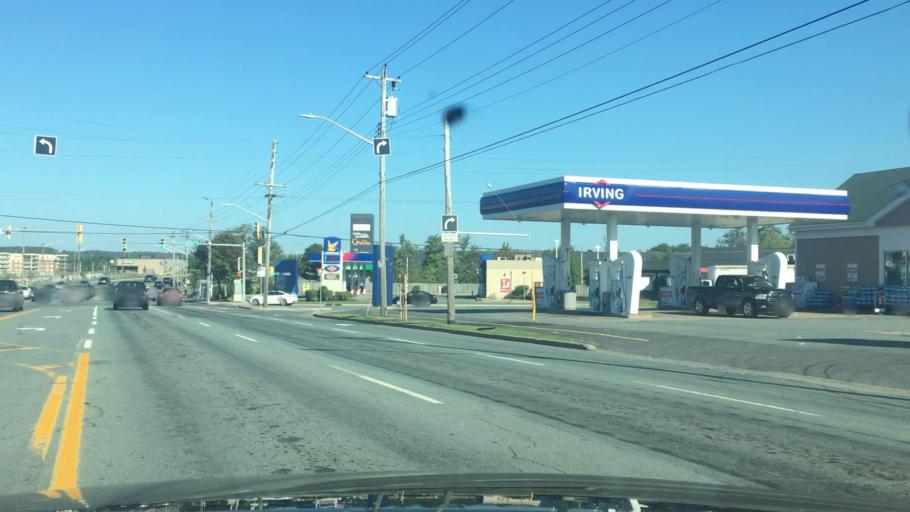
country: CA
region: Nova Scotia
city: Dartmouth
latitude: 44.6978
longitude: -63.6041
